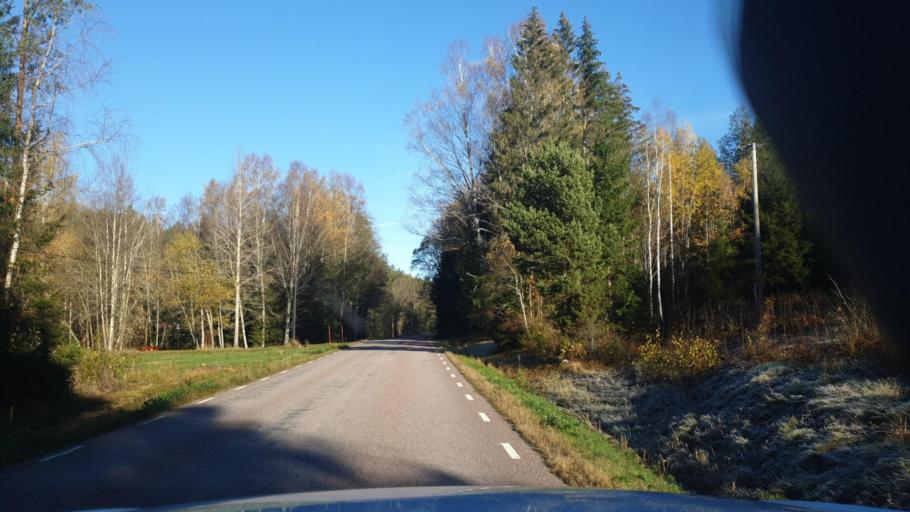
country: SE
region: Vaermland
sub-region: Grums Kommun
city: Grums
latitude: 59.4062
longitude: 13.0715
